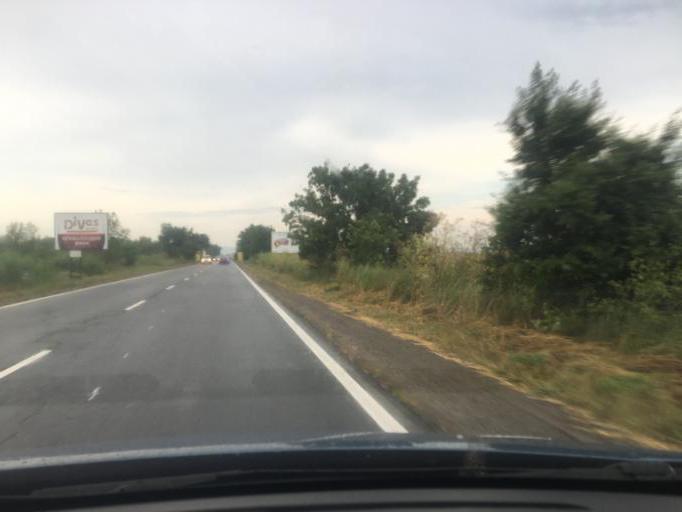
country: BG
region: Burgas
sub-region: Obshtina Pomorie
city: Pomorie
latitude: 42.5906
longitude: 27.6122
